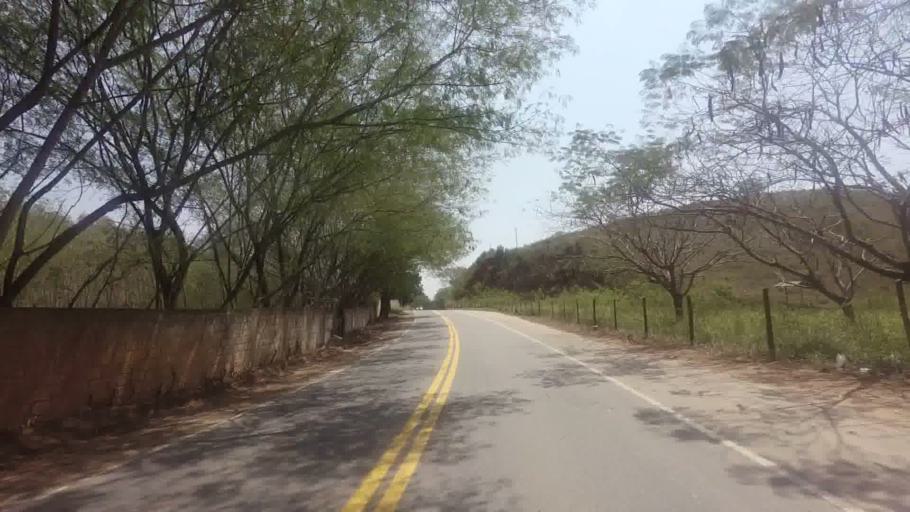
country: BR
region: Espirito Santo
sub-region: Cachoeiro De Itapemirim
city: Cachoeiro de Itapemirim
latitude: -20.8548
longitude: -41.0850
